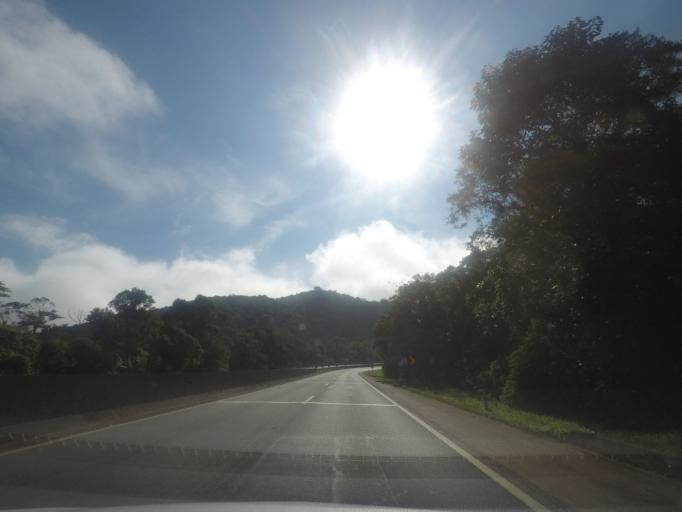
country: BR
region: Parana
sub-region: Piraquara
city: Piraquara
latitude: -25.5925
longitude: -48.8955
